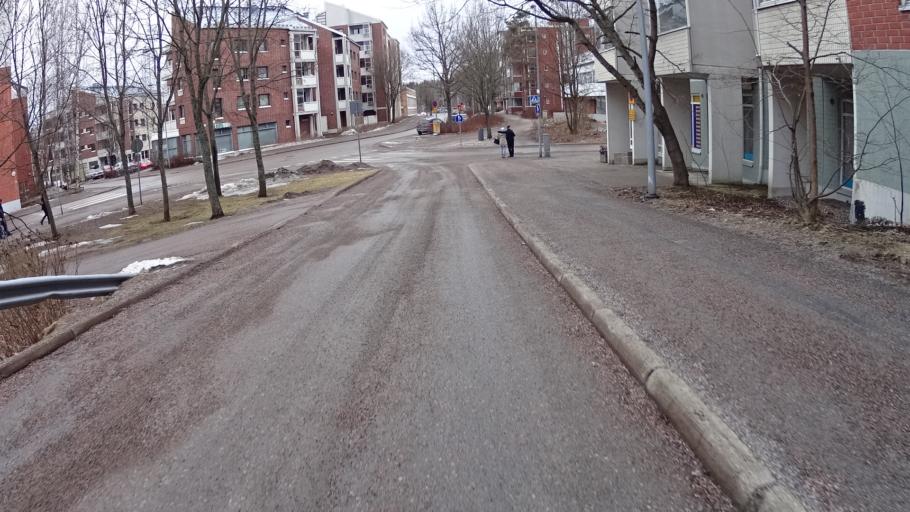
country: FI
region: Uusimaa
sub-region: Helsinki
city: Kilo
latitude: 60.2240
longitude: 24.8143
